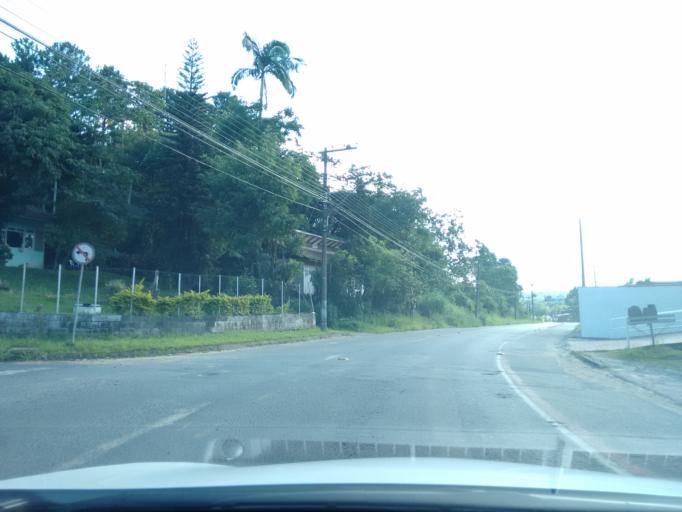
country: BR
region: Santa Catarina
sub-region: Blumenau
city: Blumenau
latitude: -26.8592
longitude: -49.0775
